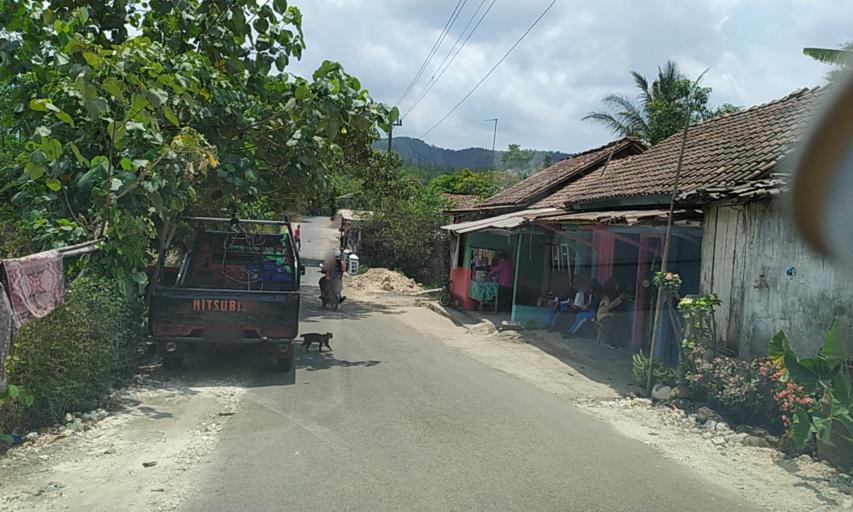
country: ID
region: Central Java
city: Cilopadang
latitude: -7.3111
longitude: 108.8012
